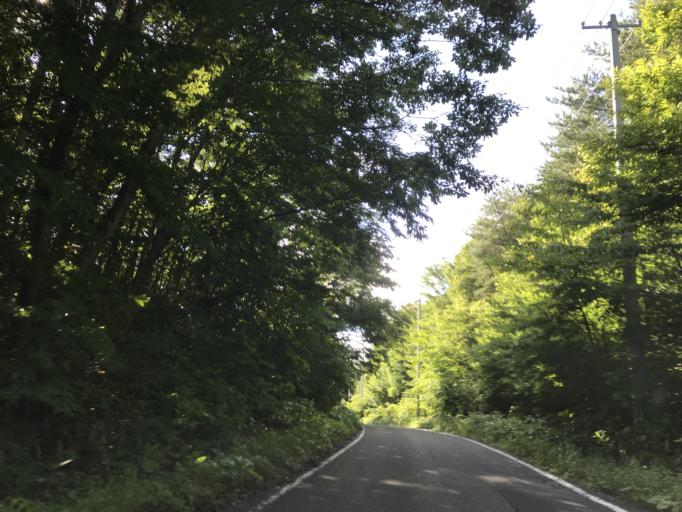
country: JP
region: Iwate
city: Ichinoseki
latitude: 38.8964
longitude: 140.8882
